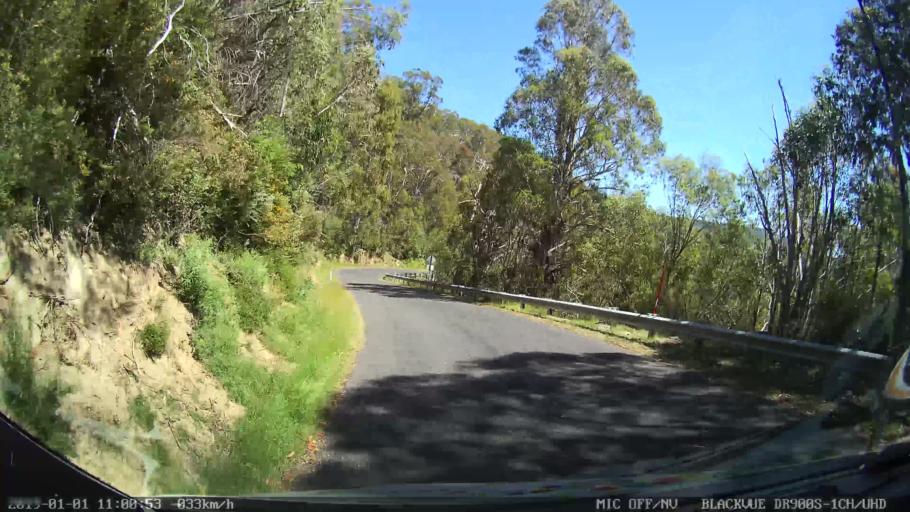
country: AU
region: New South Wales
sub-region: Snowy River
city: Jindabyne
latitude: -35.9796
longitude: 148.3981
